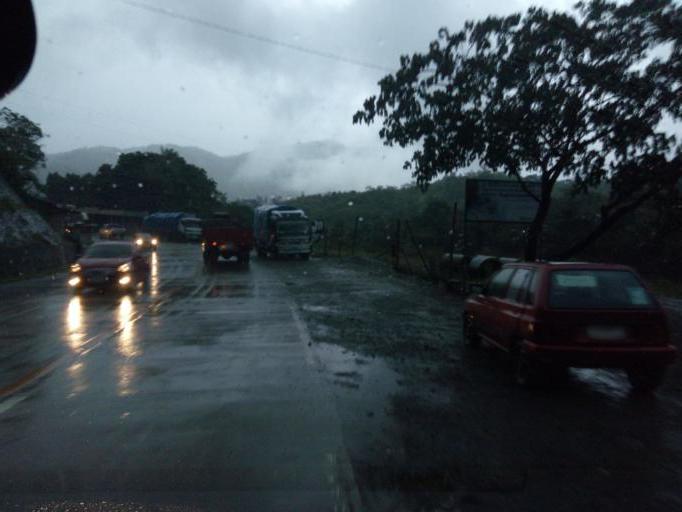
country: PH
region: Cagayan Valley
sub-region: Province of Nueva Vizcaya
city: Santa Fe
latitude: 16.1605
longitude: 120.9402
